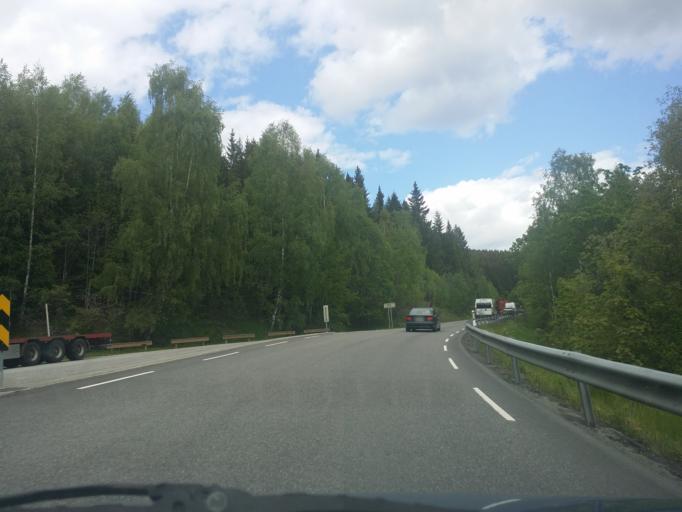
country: NO
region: Oppland
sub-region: Jevnaker
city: Jevnaker
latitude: 60.2607
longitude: 10.4411
